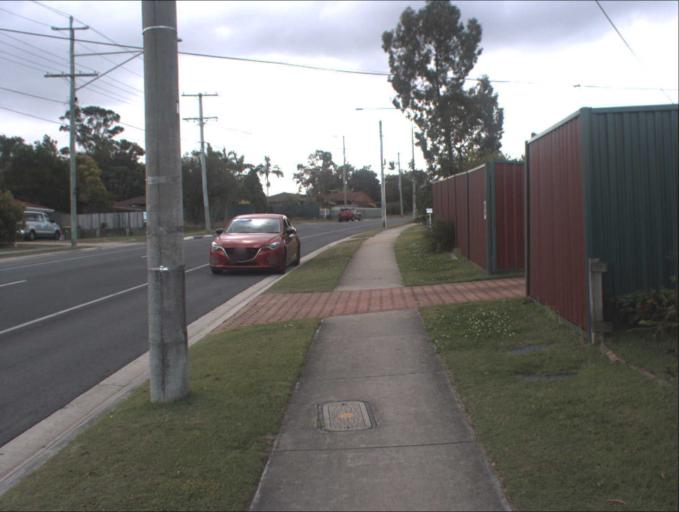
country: AU
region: Queensland
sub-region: Logan
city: Park Ridge South
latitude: -27.6729
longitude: 153.0374
